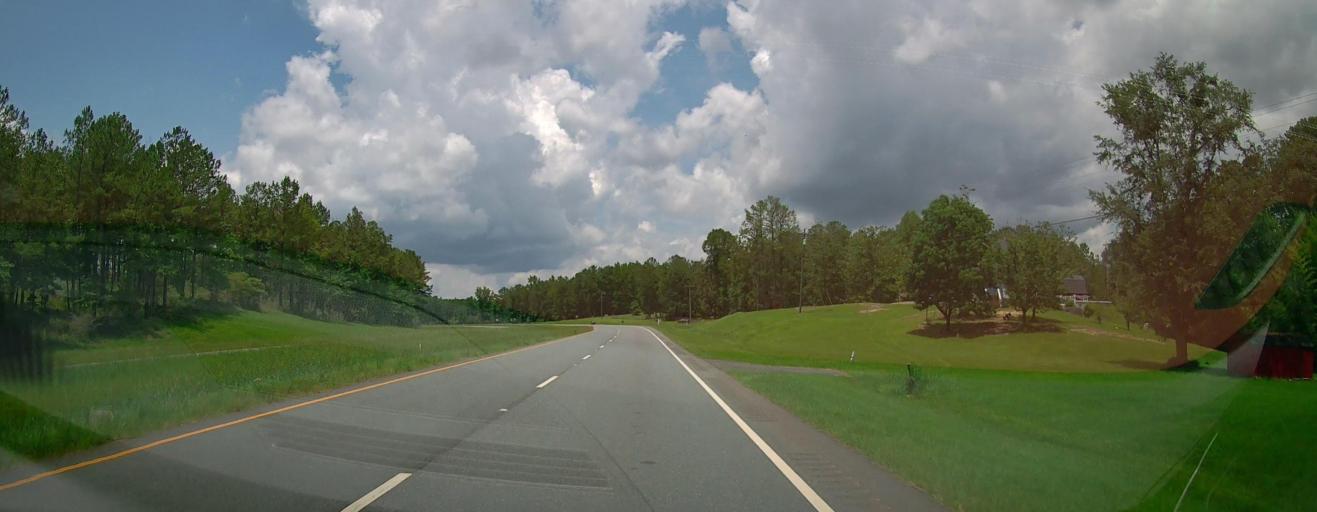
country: US
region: Georgia
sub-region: Upson County
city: Thomaston
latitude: 32.8044
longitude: -84.2766
